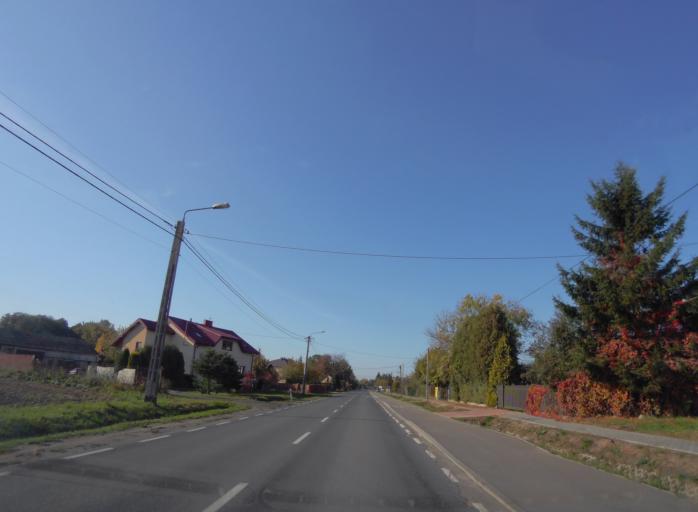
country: PL
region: Masovian Voivodeship
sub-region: Powiat minski
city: Halinow
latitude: 52.1940
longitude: 21.3658
